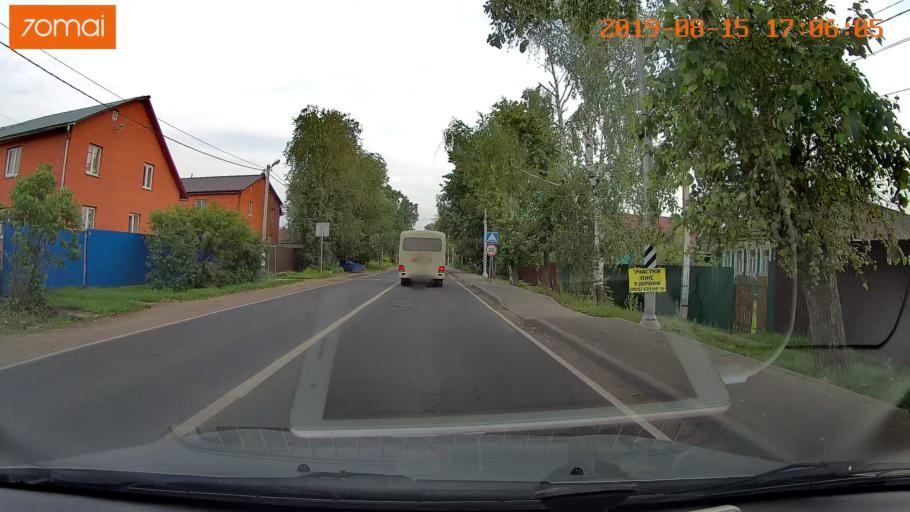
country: RU
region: Moskovskaya
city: Beloozerskiy
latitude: 55.4707
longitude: 38.4145
